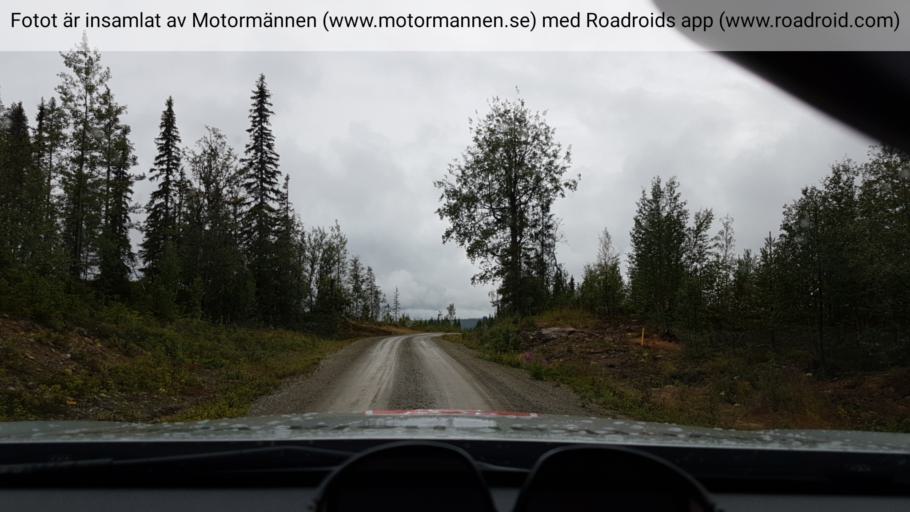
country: SE
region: Vaesterbotten
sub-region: Storumans Kommun
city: Storuman
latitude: 64.8456
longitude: 17.4091
